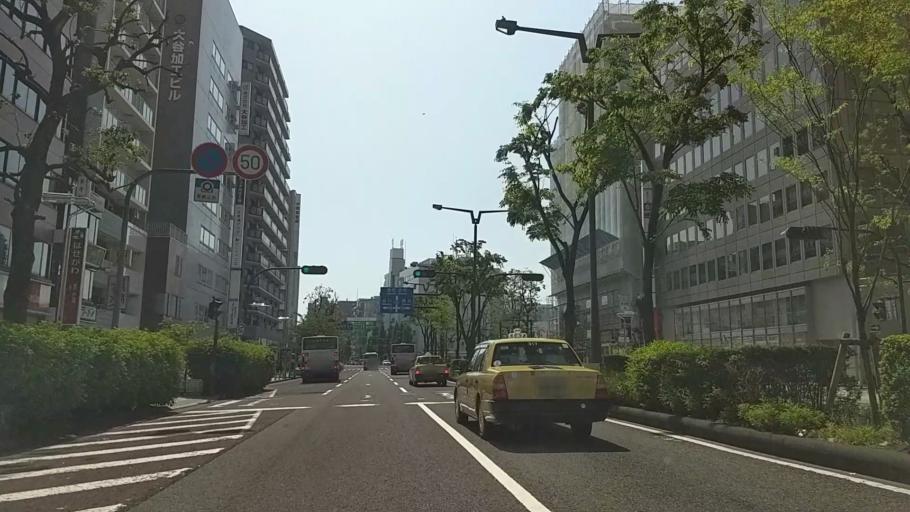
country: JP
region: Kanagawa
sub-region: Kawasaki-shi
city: Kawasaki
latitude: 35.5277
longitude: 139.7009
